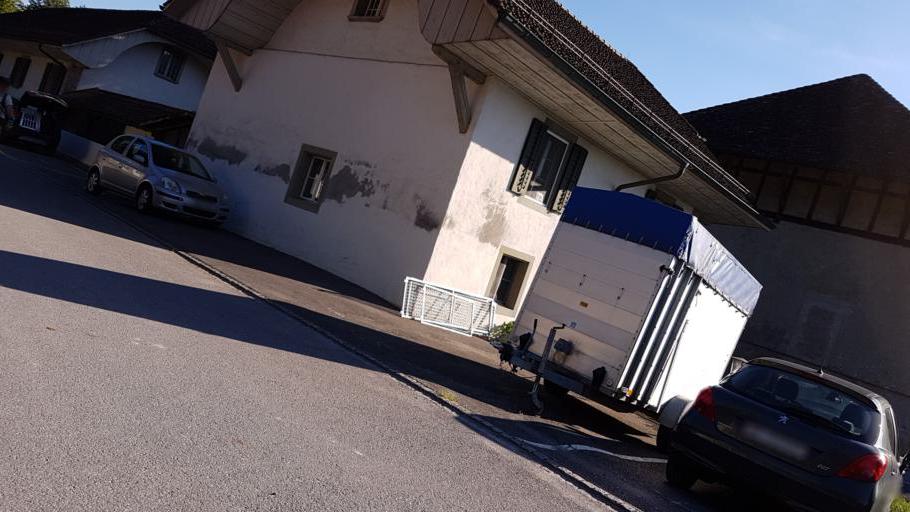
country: CH
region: Bern
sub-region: Bern-Mittelland District
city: Munsingen
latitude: 46.8894
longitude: 7.5589
